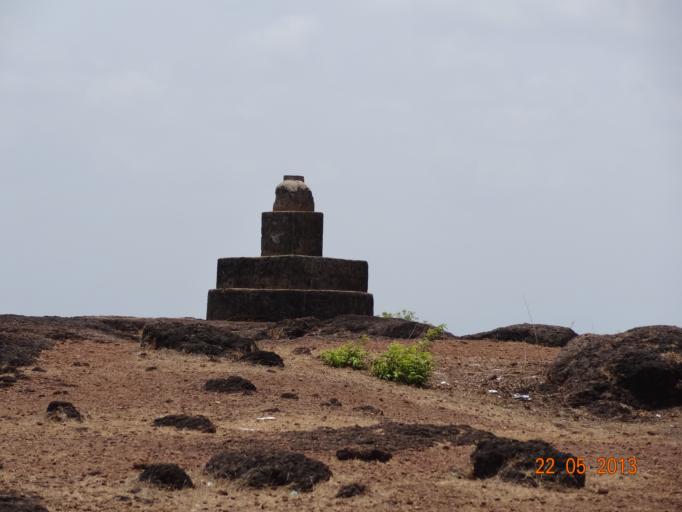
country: IN
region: Goa
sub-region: North Goa
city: Vagator
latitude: 15.6053
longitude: 73.7362
